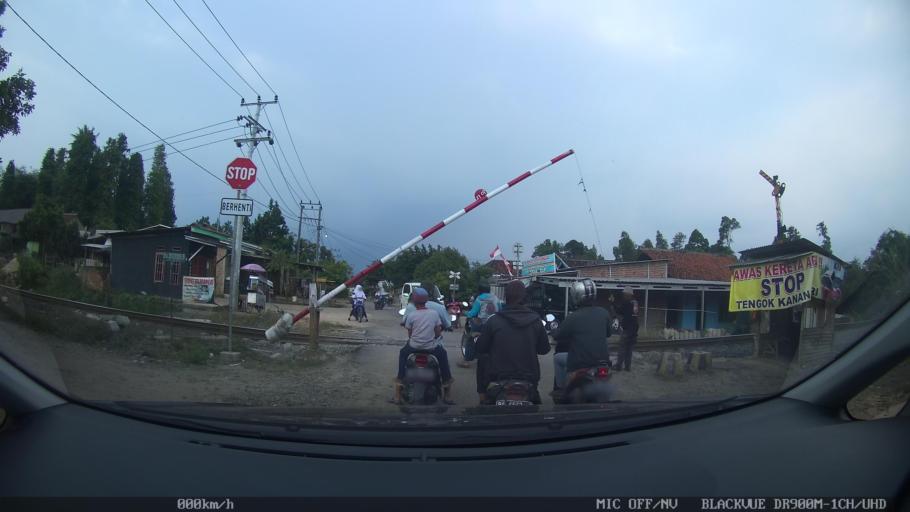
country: ID
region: Lampung
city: Kedaton
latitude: -5.3495
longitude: 105.2300
